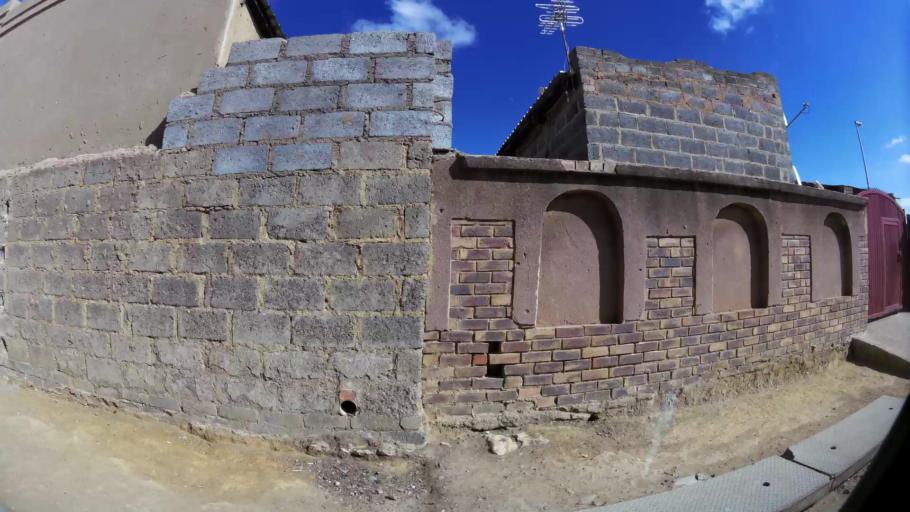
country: ZA
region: Gauteng
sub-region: City of Johannesburg Metropolitan Municipality
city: Modderfontein
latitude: -26.0417
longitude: 28.1809
